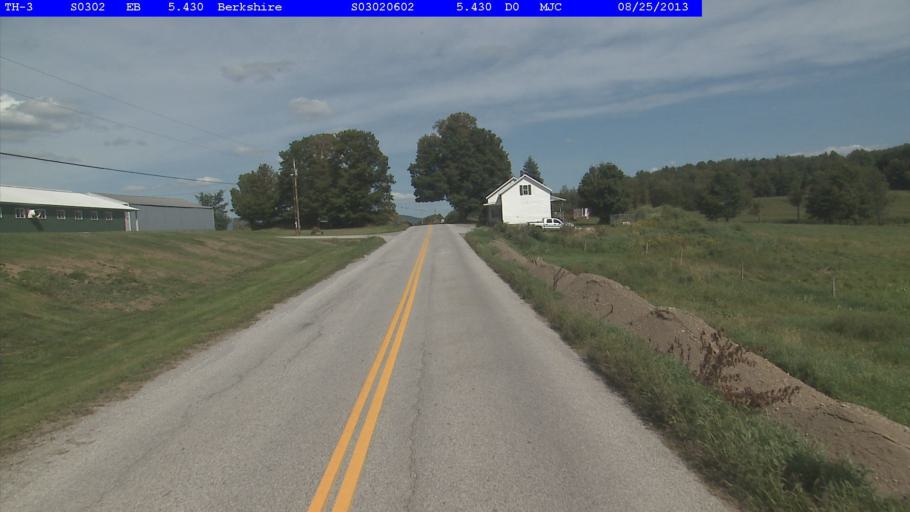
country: US
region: Vermont
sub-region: Franklin County
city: Richford
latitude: 44.9848
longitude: -72.7127
